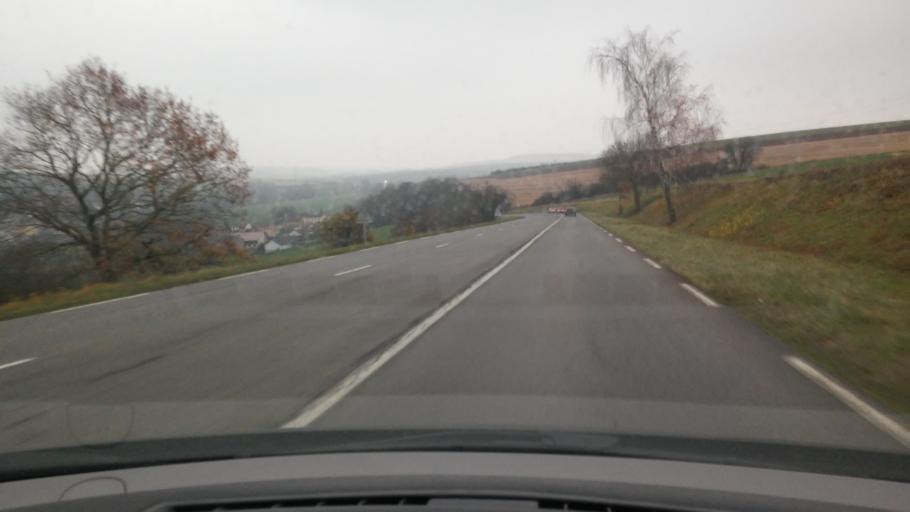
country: FR
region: Lorraine
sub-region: Departement de la Moselle
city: Courcelles-Chaussy
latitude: 49.1065
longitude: 6.4687
